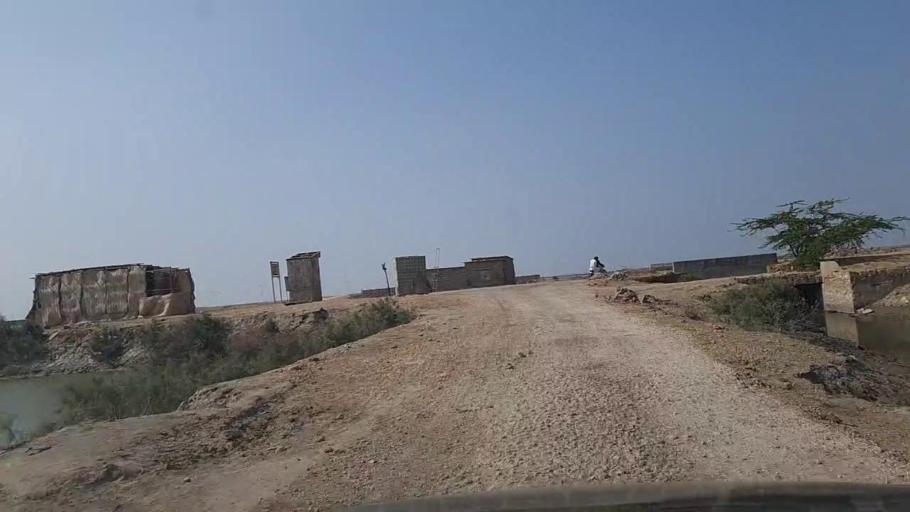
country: PK
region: Sindh
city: Gharo
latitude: 24.7073
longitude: 67.5362
